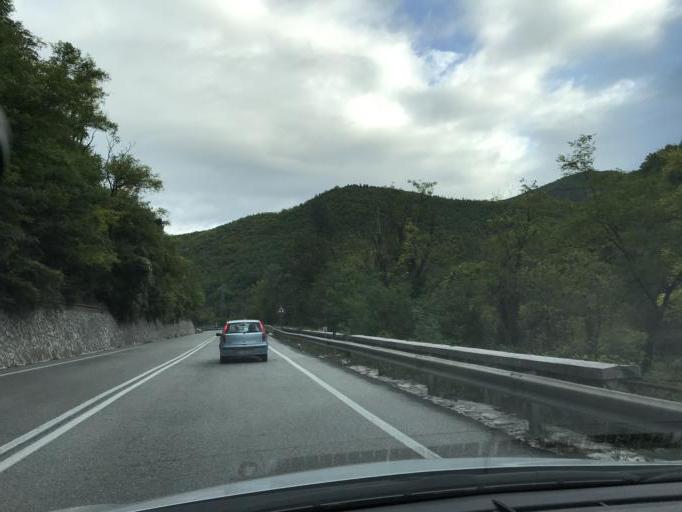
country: IT
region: Umbria
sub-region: Provincia di Perugia
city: Spoleto
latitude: 42.6796
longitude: 12.7259
